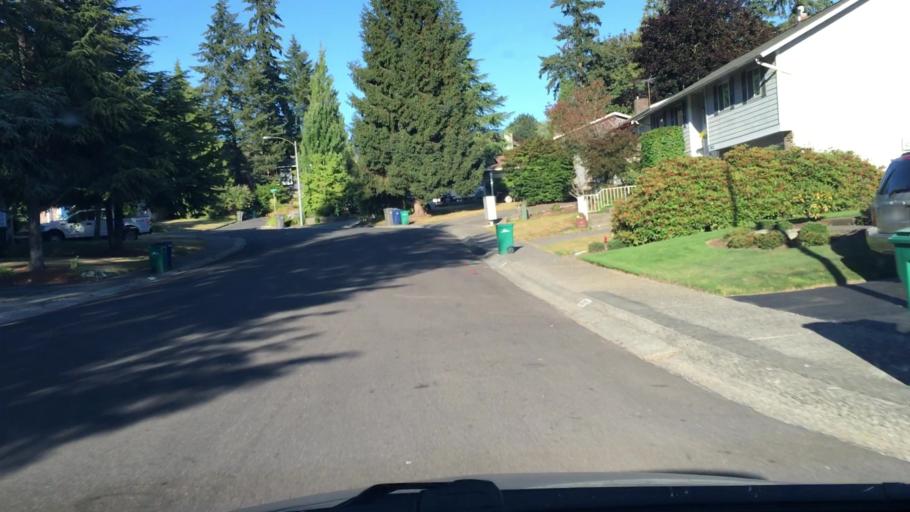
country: US
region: Washington
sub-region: King County
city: Kingsgate
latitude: 47.7280
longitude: -122.1718
